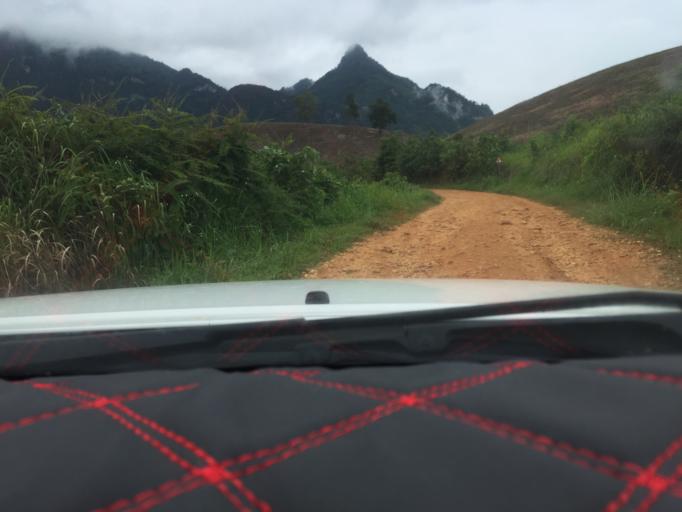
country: TH
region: Phayao
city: Phu Sang
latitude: 19.7697
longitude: 100.4968
